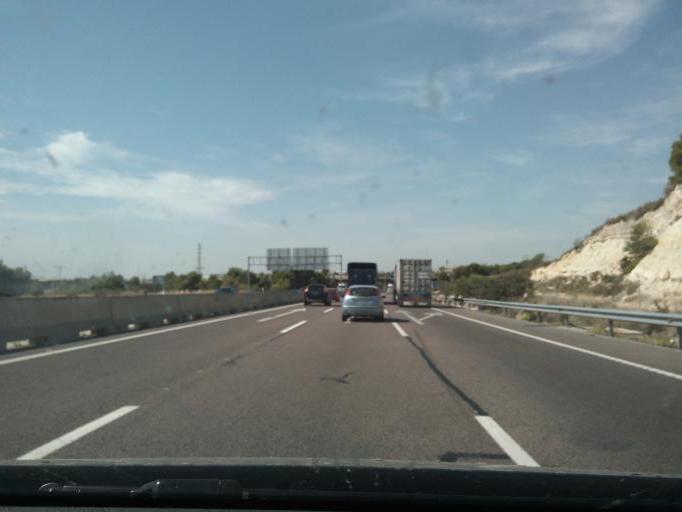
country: ES
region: Valencia
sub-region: Provincia de Valencia
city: Manises
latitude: 39.5285
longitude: -0.4651
